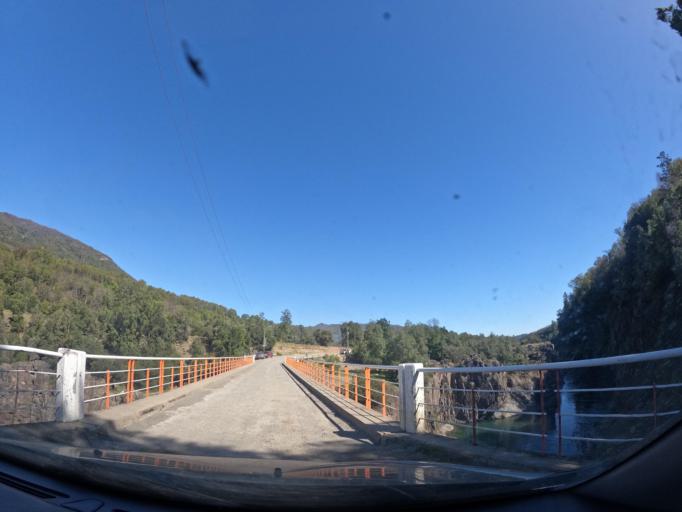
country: CL
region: Maule
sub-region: Provincia de Linares
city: Longavi
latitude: -36.2297
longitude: -71.4017
